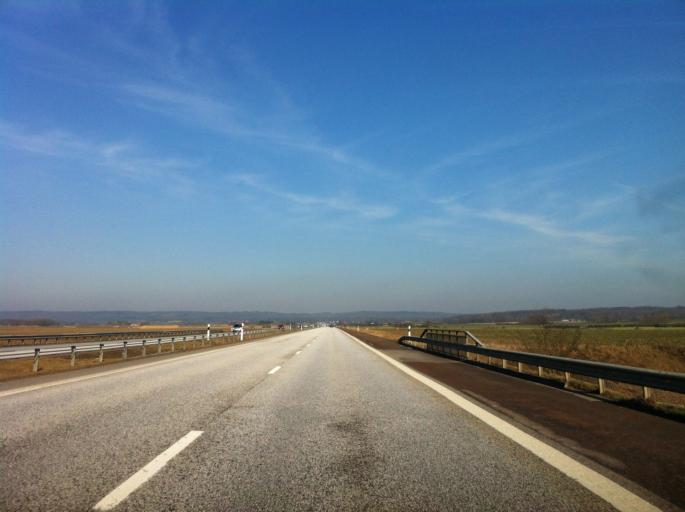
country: SE
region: Skane
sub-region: Angelholms Kommun
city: AEngelholm
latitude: 56.2836
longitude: 12.8995
